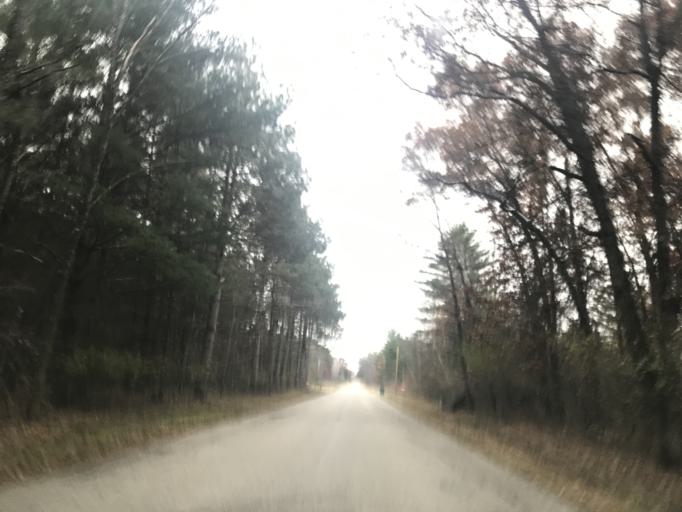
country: US
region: Wisconsin
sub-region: Marinette County
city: Peshtigo
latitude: 45.1145
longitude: -87.7499
